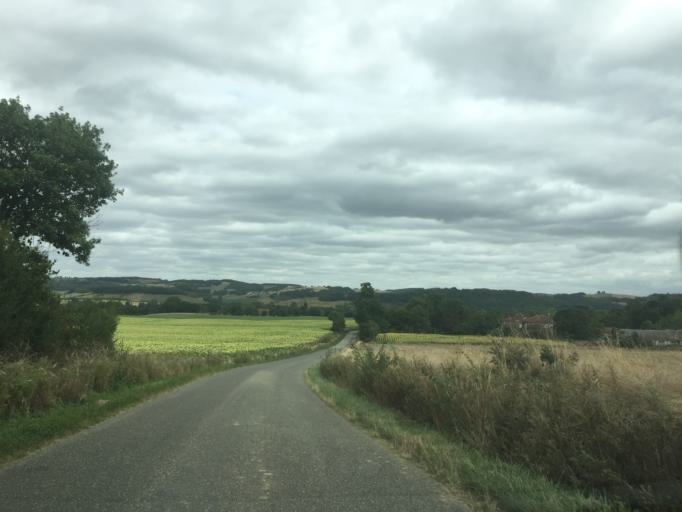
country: FR
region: Midi-Pyrenees
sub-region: Departement du Gers
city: Vic-Fezensac
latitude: 43.6698
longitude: 0.3801
